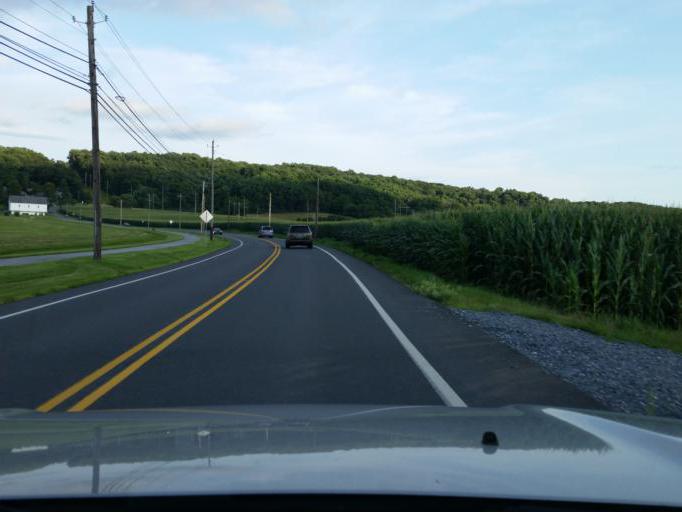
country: US
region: Pennsylvania
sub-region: Dauphin County
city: Hummelstown
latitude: 40.2561
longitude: -76.6983
